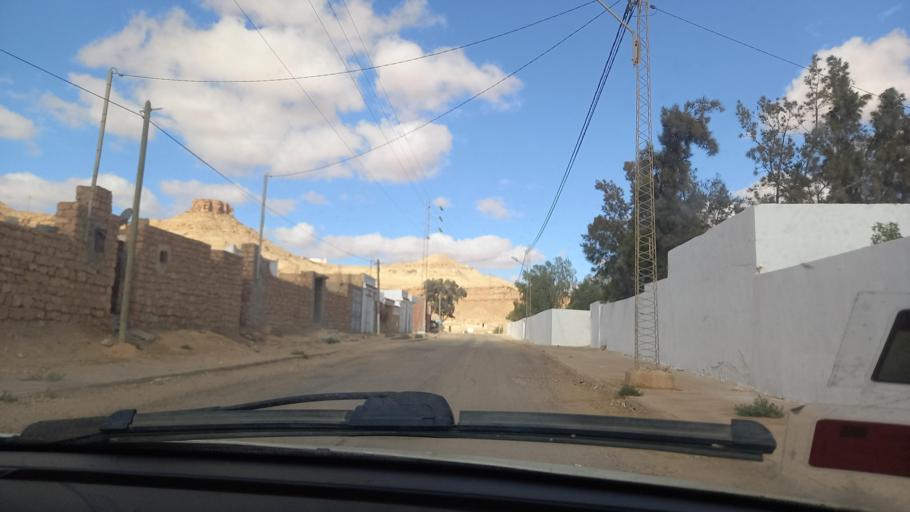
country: TN
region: Tataouine
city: Tataouine
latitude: 32.9831
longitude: 10.2622
